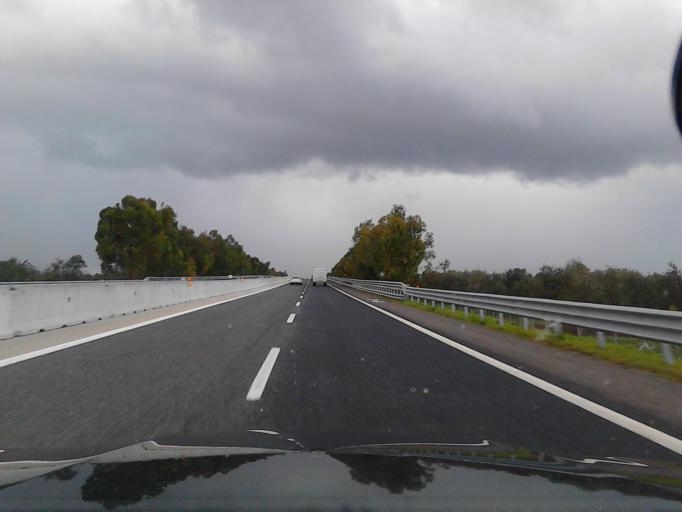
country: IT
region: Apulia
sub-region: Provincia di Bari
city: Bitonto
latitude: 41.1253
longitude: 16.7215
